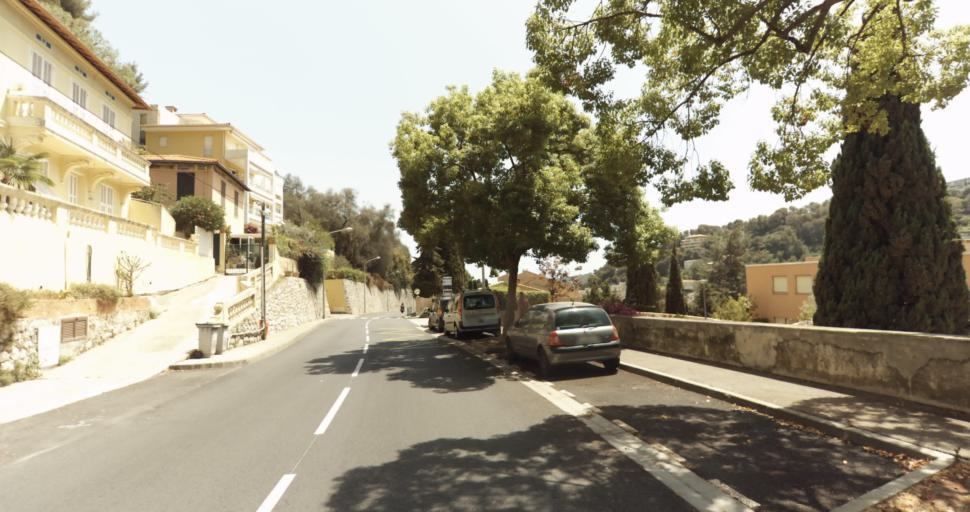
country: FR
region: Provence-Alpes-Cote d'Azur
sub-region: Departement des Alpes-Maritimes
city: Roquebrune-Cap-Martin
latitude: 43.7707
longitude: 7.4793
